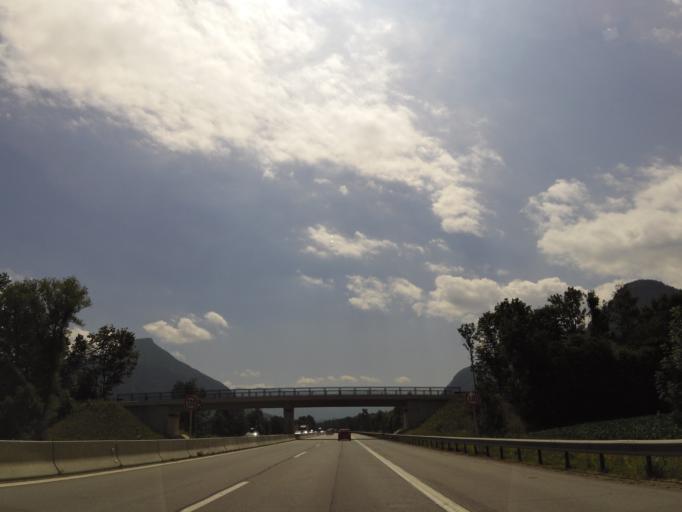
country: DE
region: Bavaria
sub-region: Upper Bavaria
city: Flintsbach
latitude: 47.7301
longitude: 12.1338
